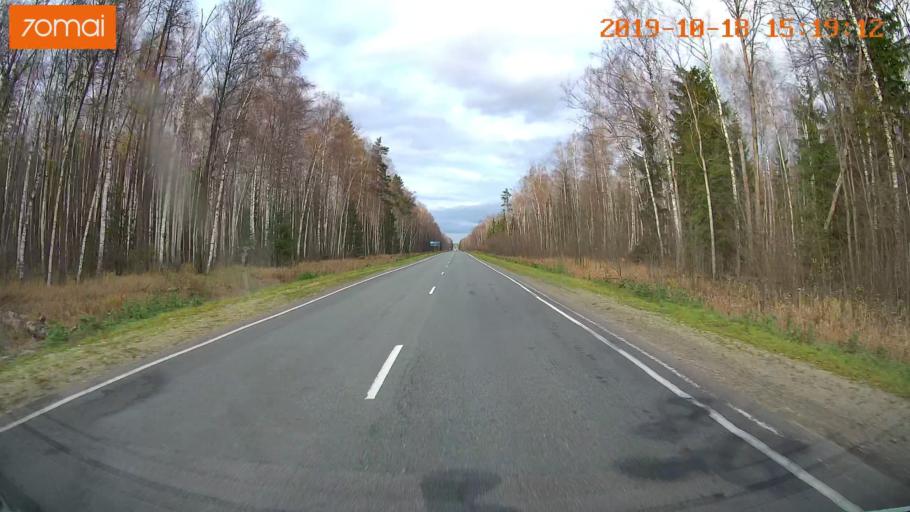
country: RU
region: Vladimir
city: Anopino
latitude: 55.6696
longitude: 40.7359
